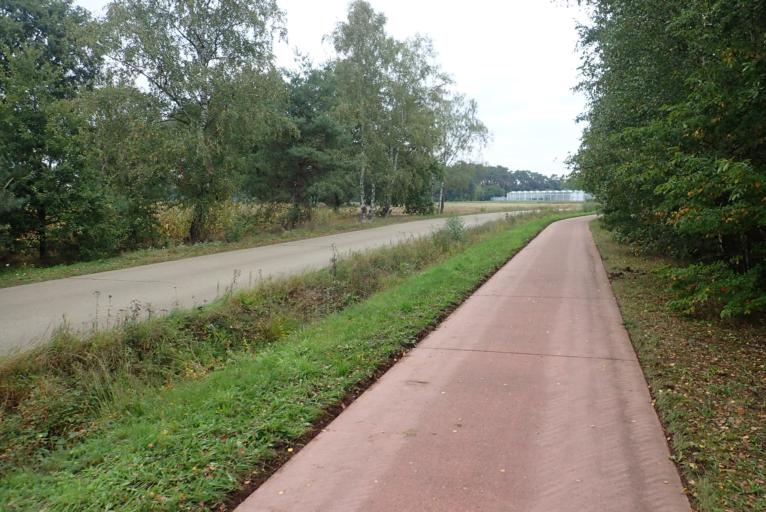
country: BE
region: Flanders
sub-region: Provincie Antwerpen
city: Lille
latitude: 51.2254
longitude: 4.8010
